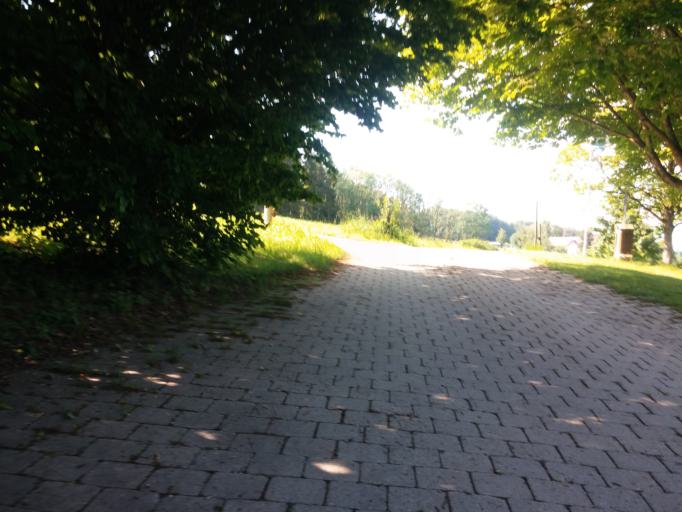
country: DE
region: Bavaria
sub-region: Swabia
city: Woringen
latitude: 47.8808
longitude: 10.2025
